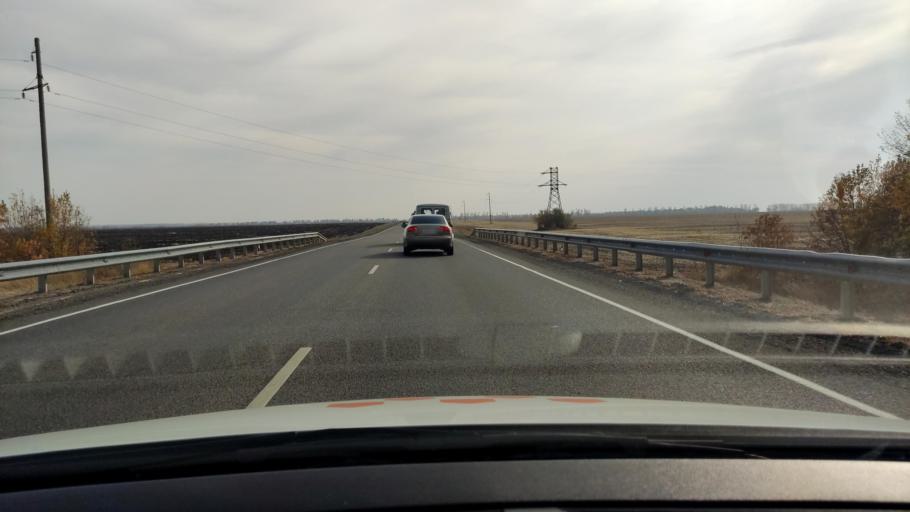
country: RU
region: Voronezj
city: Volya
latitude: 51.6886
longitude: 39.5103
